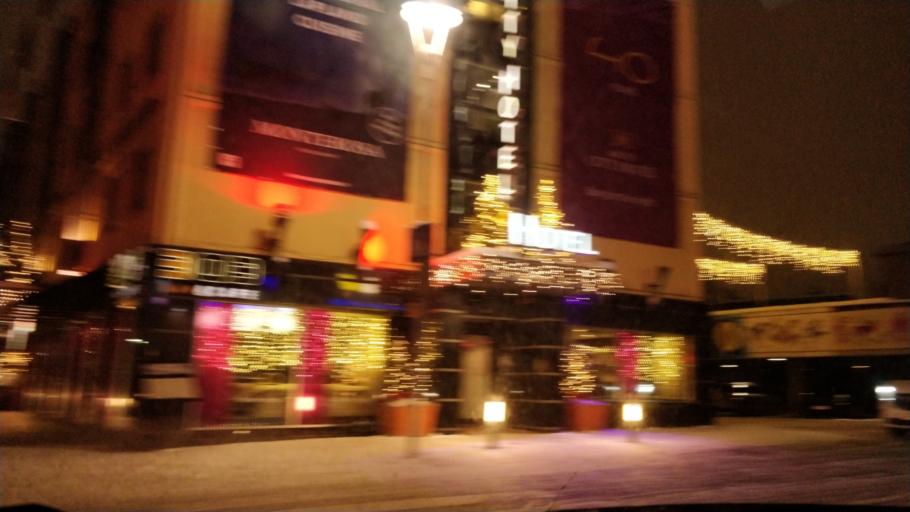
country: FI
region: Lapland
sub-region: Rovaniemi
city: Rovaniemi
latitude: 66.5015
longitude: 25.7301
